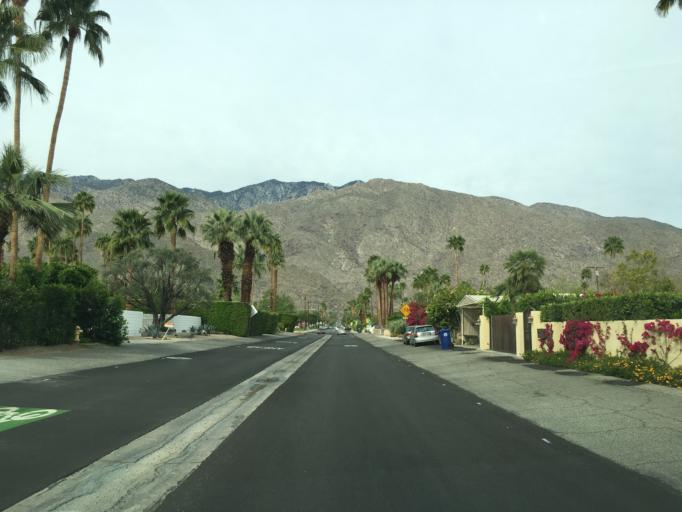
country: US
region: California
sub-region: Riverside County
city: Palm Springs
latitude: 33.8087
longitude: -116.5348
